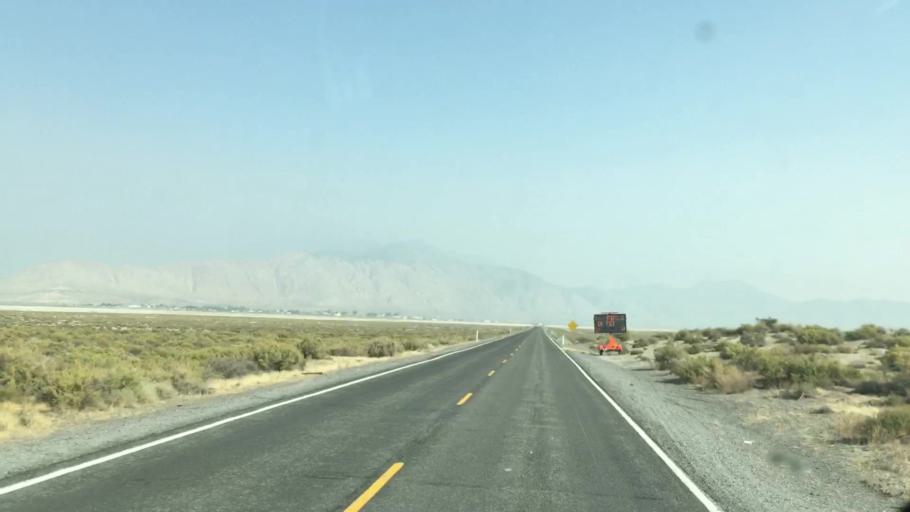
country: US
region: Nevada
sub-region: Pershing County
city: Lovelock
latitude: 40.6260
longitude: -119.3364
